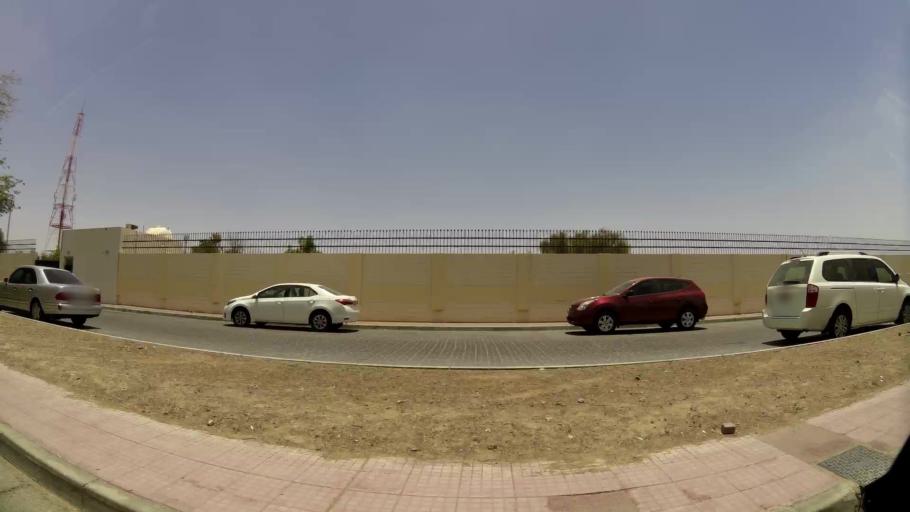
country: OM
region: Al Buraimi
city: Al Buraymi
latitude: 24.2613
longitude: 55.7375
